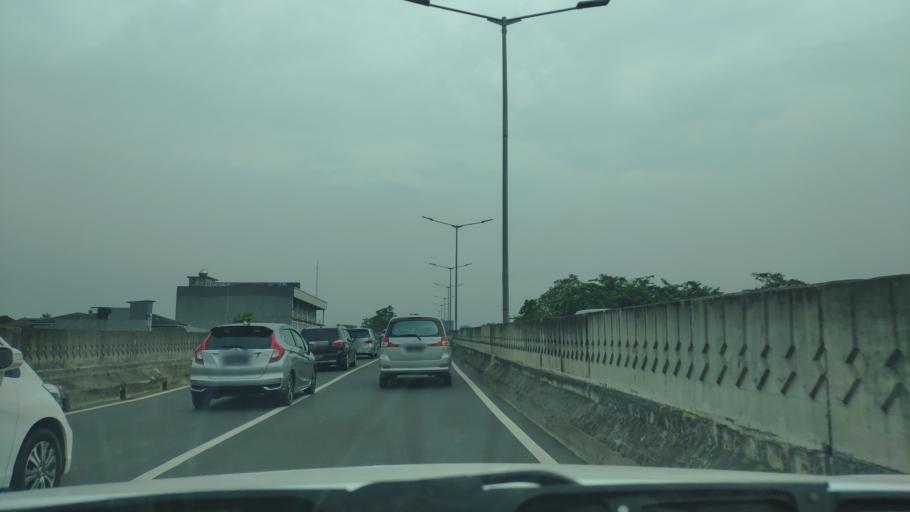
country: ID
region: Jakarta Raya
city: Jakarta
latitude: -6.2703
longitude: 106.8087
